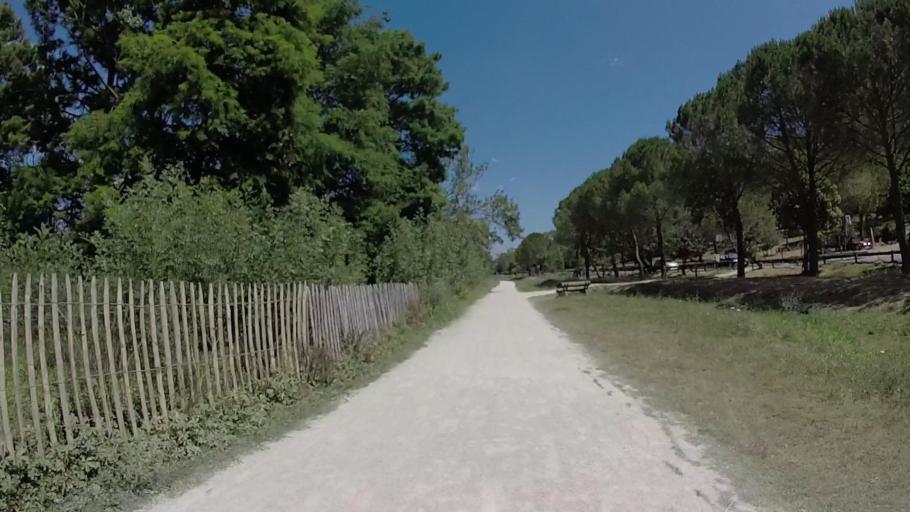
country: FR
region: Provence-Alpes-Cote d'Azur
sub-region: Departement des Alpes-Maritimes
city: Mougins
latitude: 43.5969
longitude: 7.0122
